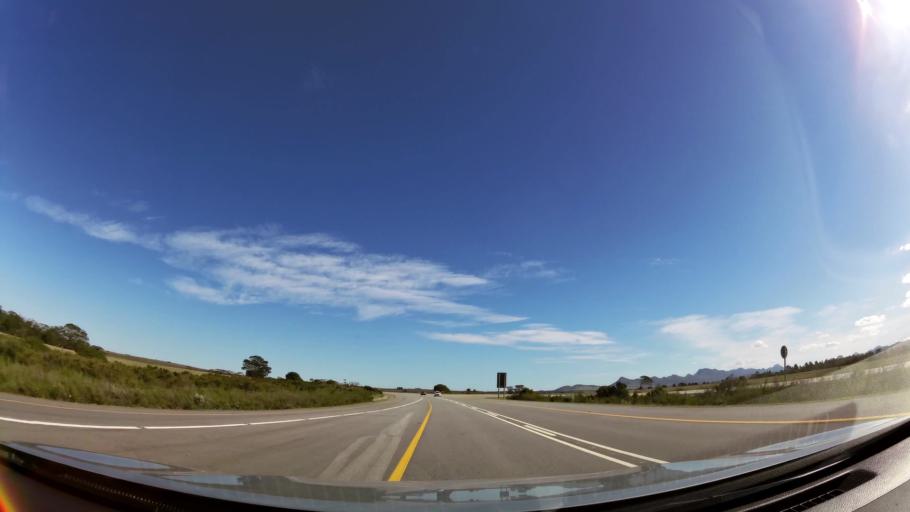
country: ZA
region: Eastern Cape
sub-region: Cacadu District Municipality
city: Kruisfontein
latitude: -34.0303
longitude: 24.5979
